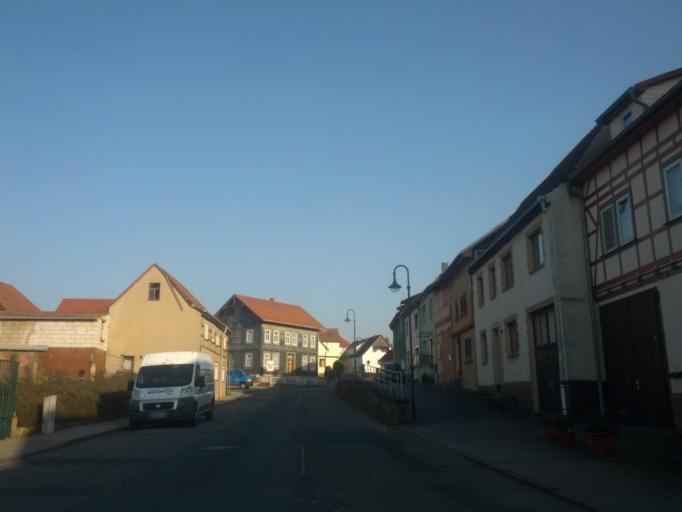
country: DE
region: Thuringia
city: Mihla
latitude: 51.0765
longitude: 10.3382
